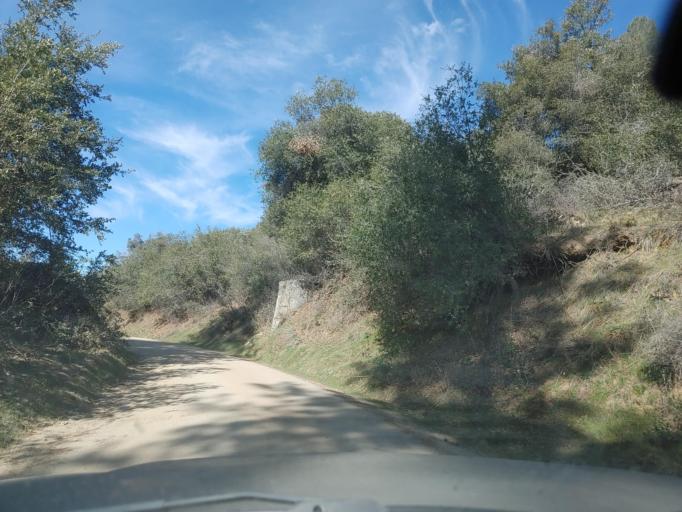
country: US
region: California
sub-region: Madera County
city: Ahwahnee
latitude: 37.4173
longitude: -119.7068
